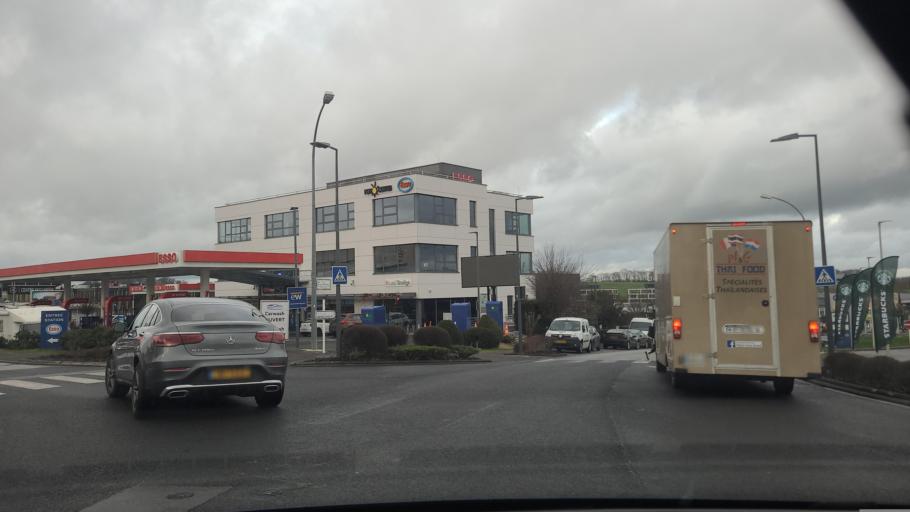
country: LU
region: Luxembourg
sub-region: Canton d'Esch-sur-Alzette
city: Leudelange
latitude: 49.5666
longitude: 6.0800
